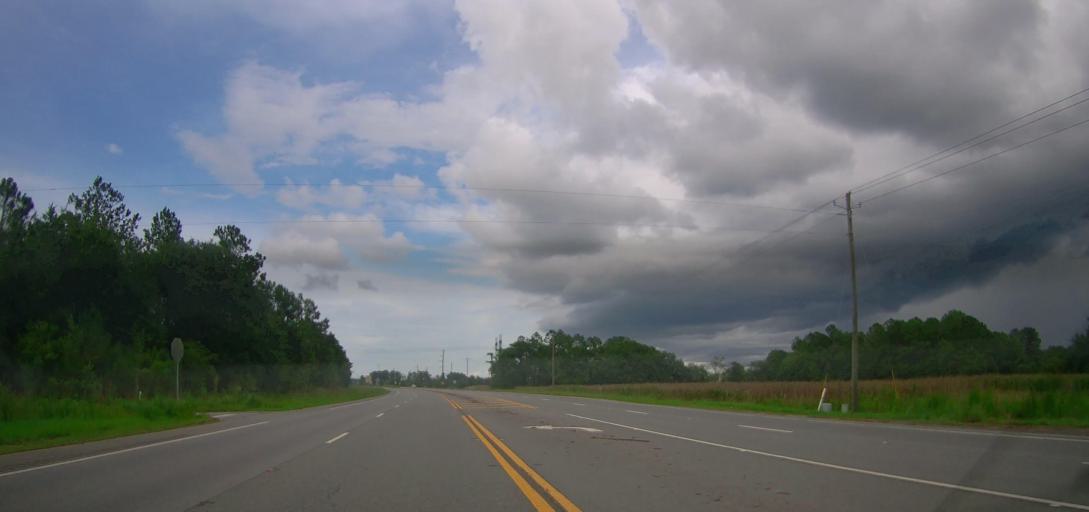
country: US
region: Georgia
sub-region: Pierce County
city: Blackshear
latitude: 31.4124
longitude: -82.1083
